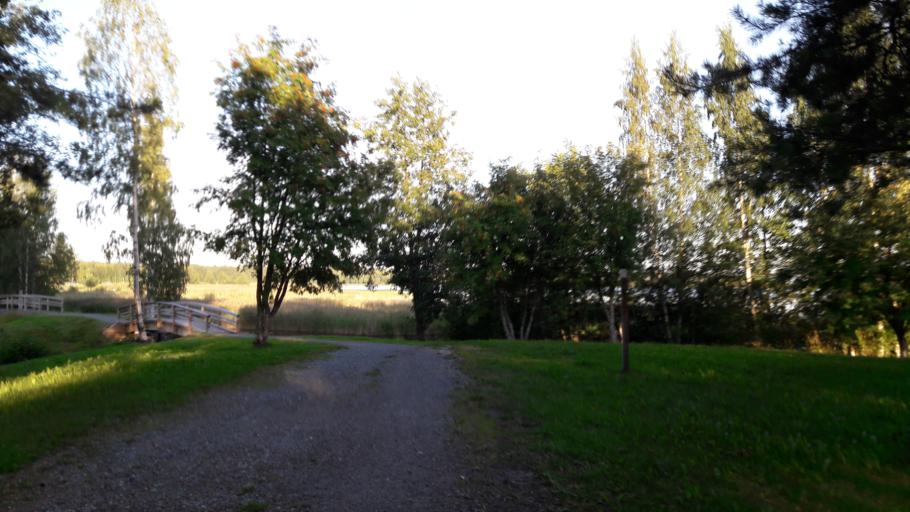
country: FI
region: North Karelia
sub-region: Joensuu
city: Joensuu
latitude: 62.6131
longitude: 29.6972
